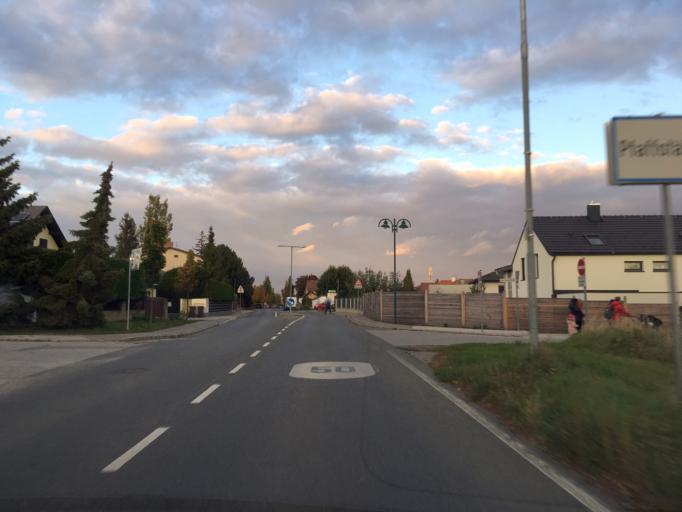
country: AT
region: Lower Austria
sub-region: Politischer Bezirk Baden
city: Pfaffstatten
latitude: 48.0159
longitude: 16.2539
